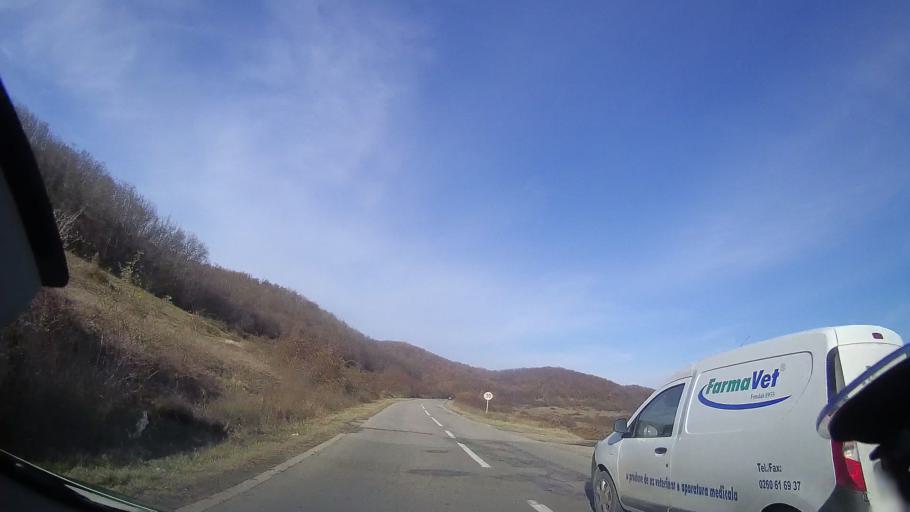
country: RO
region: Bihor
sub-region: Comuna Tileagd
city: Tileagd
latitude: 47.0894
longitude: 22.2353
